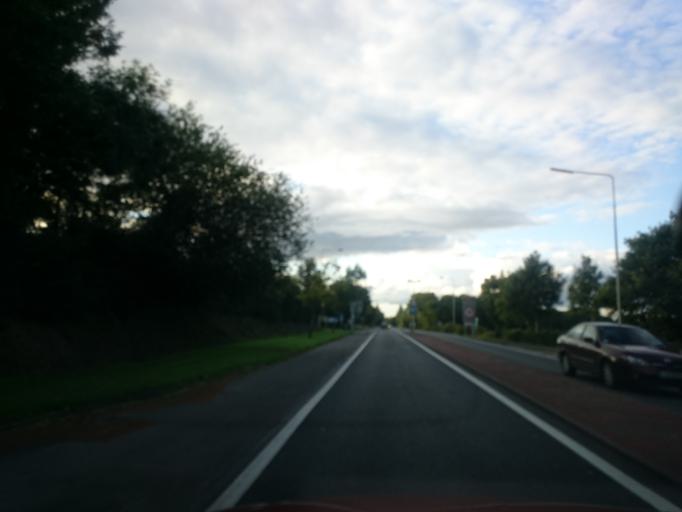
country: IE
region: Leinster
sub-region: Loch Garman
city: Enniscorthy
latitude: 52.4267
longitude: -6.5321
